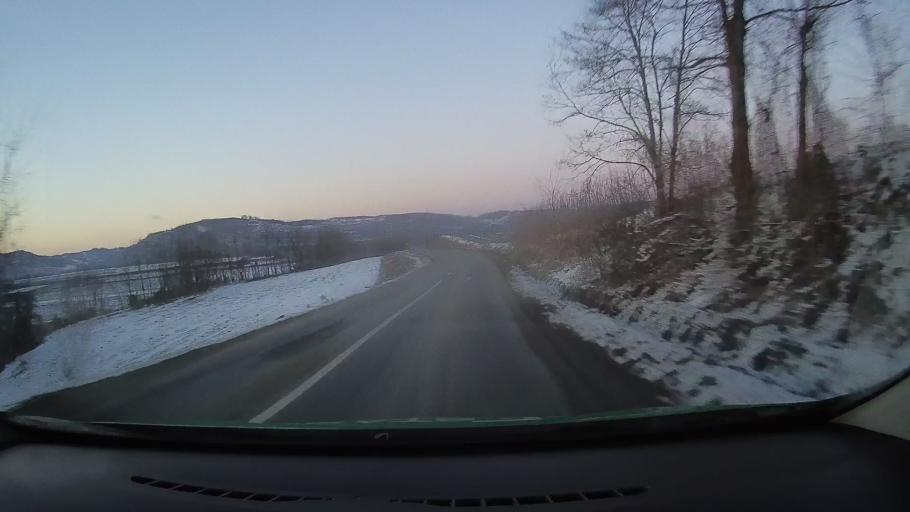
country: RO
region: Sibiu
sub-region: Comuna Alma
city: Alma
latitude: 46.1900
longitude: 24.4704
